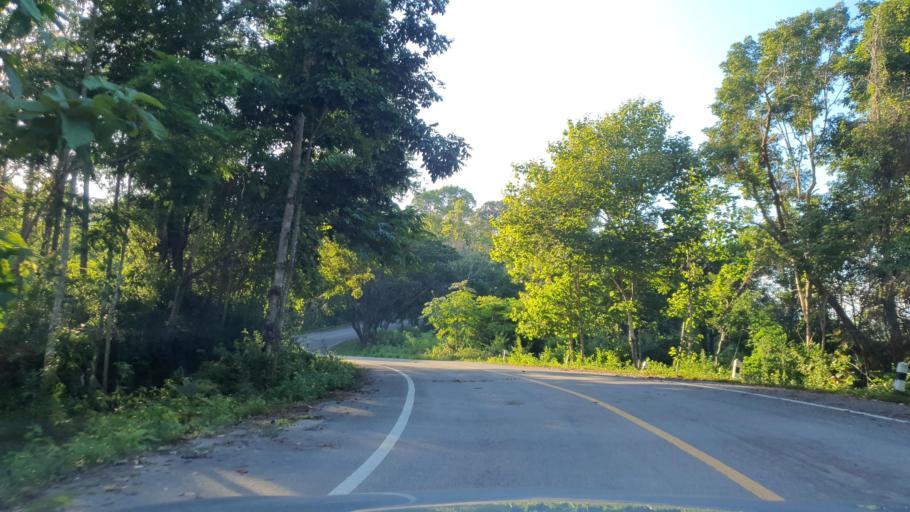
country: TH
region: Chiang Mai
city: Mae On
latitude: 18.8075
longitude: 99.3036
